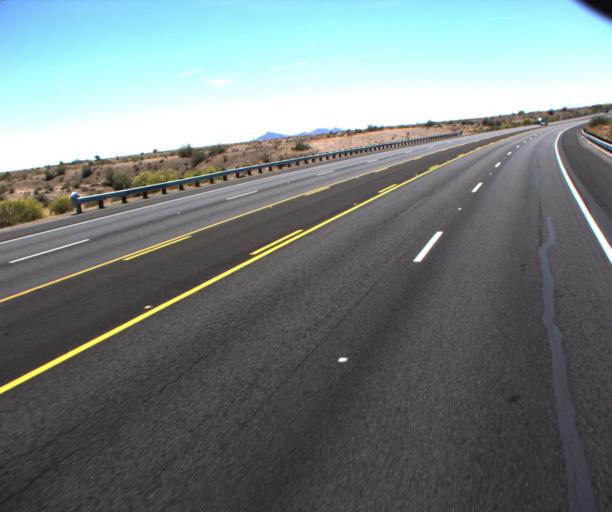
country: US
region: Arizona
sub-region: La Paz County
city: Cienega Springs
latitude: 34.1675
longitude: -114.2526
